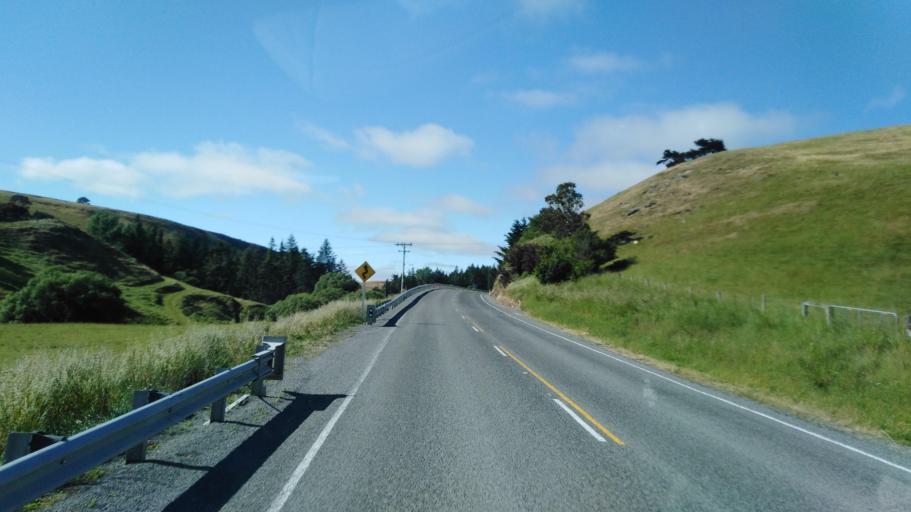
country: NZ
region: Canterbury
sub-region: Hurunui District
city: Amberley
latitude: -43.0095
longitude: 172.7022
